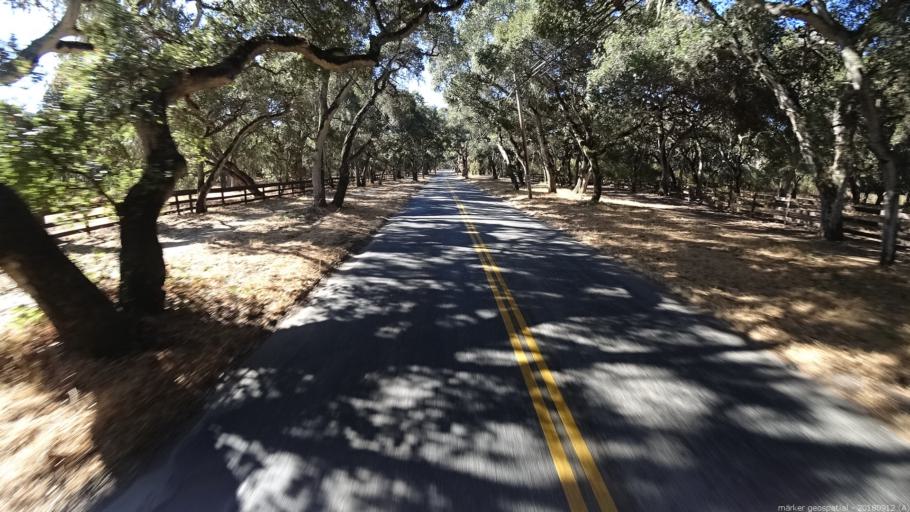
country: US
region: California
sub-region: Monterey County
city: Carmel Valley Village
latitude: 36.5540
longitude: -121.7320
